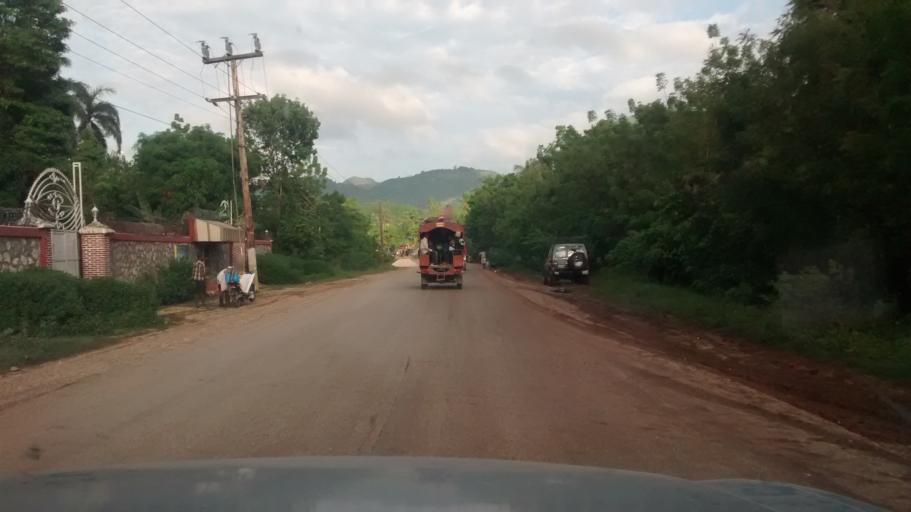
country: HT
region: Ouest
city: Tigwav
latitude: 18.4226
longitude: -72.9697
